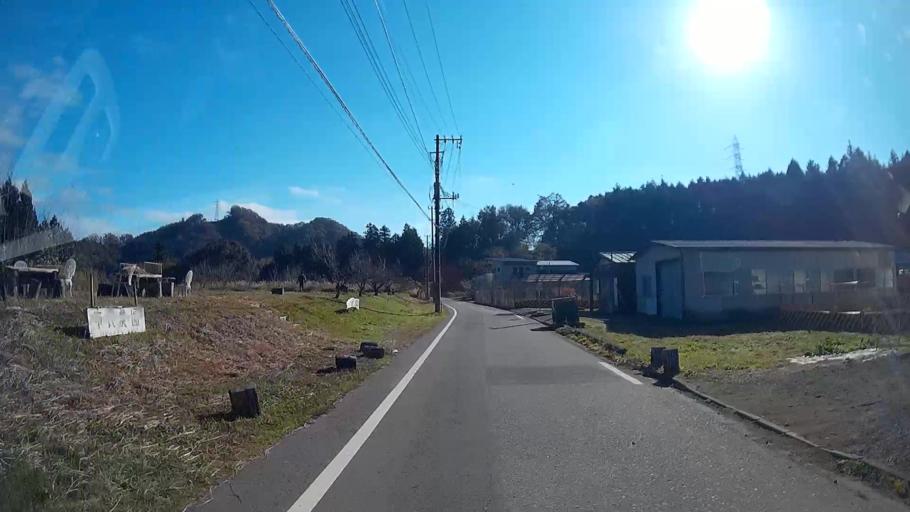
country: JP
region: Yamanashi
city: Uenohara
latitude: 35.5889
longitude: 139.1311
